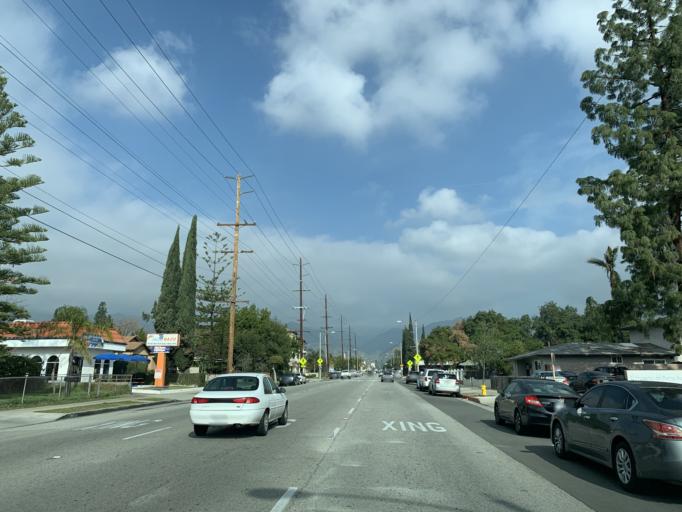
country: US
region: California
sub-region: Los Angeles County
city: Azusa
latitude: 34.1235
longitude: -117.9075
